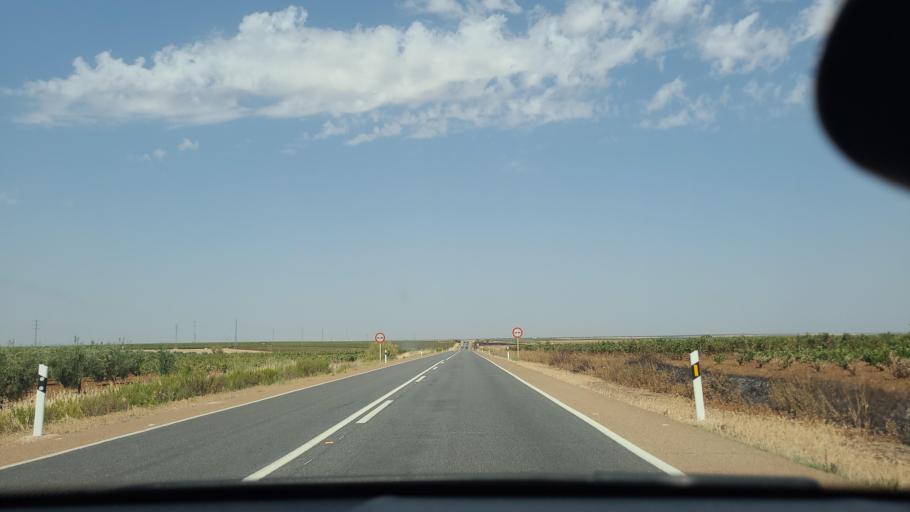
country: ES
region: Extremadura
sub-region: Provincia de Badajoz
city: Santa Marta
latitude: 38.6327
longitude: -6.6771
